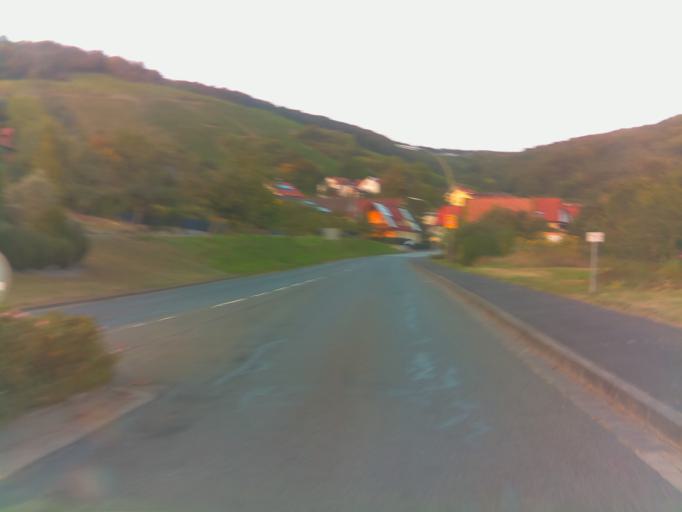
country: DE
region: Bavaria
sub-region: Regierungsbezirk Unterfranken
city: Ramsthal
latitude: 50.1383
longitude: 10.0641
